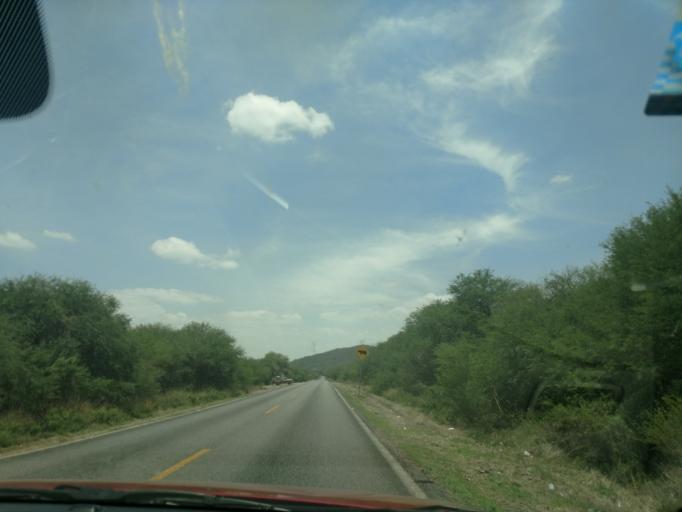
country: MX
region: San Luis Potosi
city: Ciudad Fernandez
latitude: 22.0014
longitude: -100.1434
